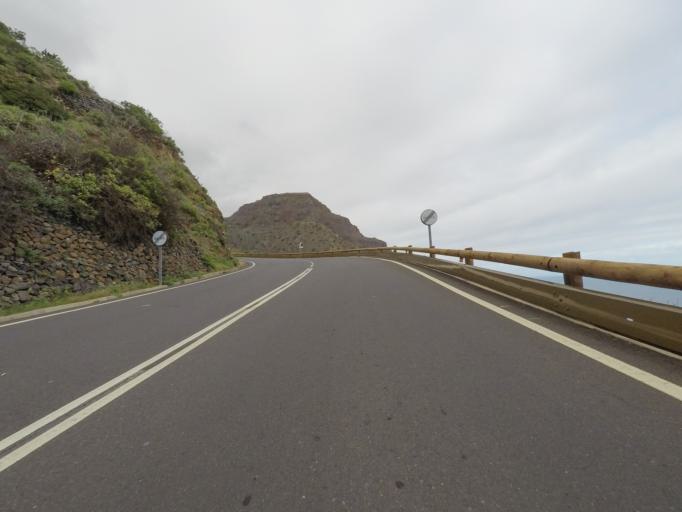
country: ES
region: Canary Islands
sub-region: Provincia de Santa Cruz de Tenerife
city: Agulo
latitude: 28.1919
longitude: -17.2004
